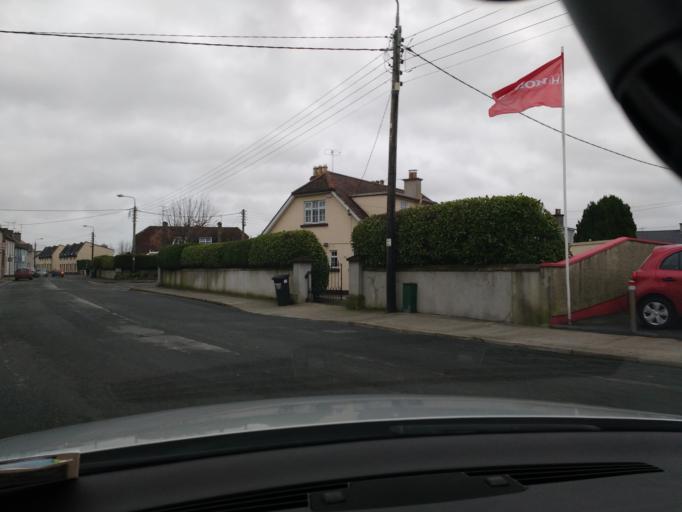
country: IE
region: Munster
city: Thurles
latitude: 52.6751
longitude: -7.8171
